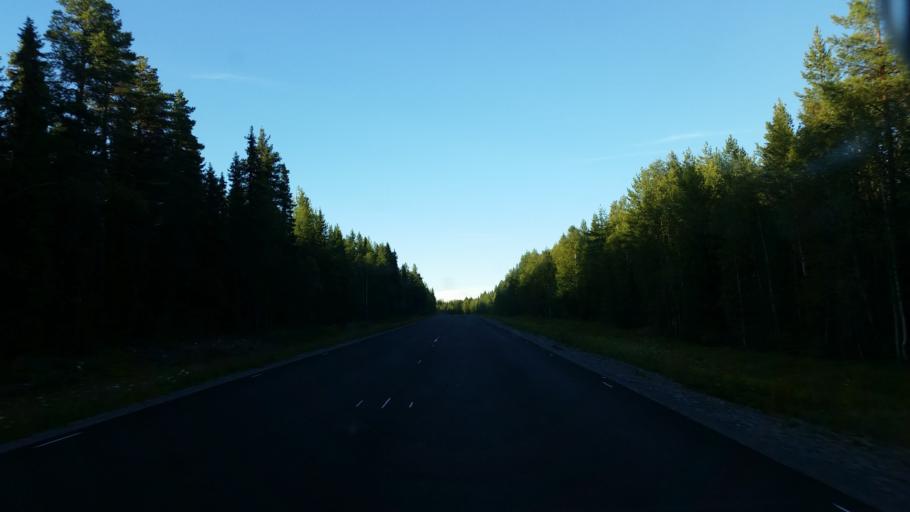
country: SE
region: Vaesterbotten
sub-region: Dorotea Kommun
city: Dorotea
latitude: 64.3065
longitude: 16.5960
